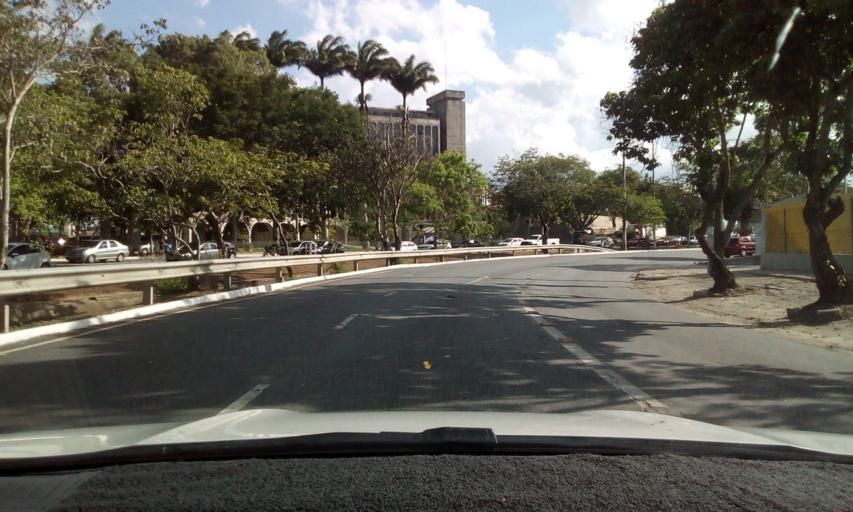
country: BR
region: Paraiba
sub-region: Campina Grande
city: Campina Grande
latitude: -7.2214
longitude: -35.8753
